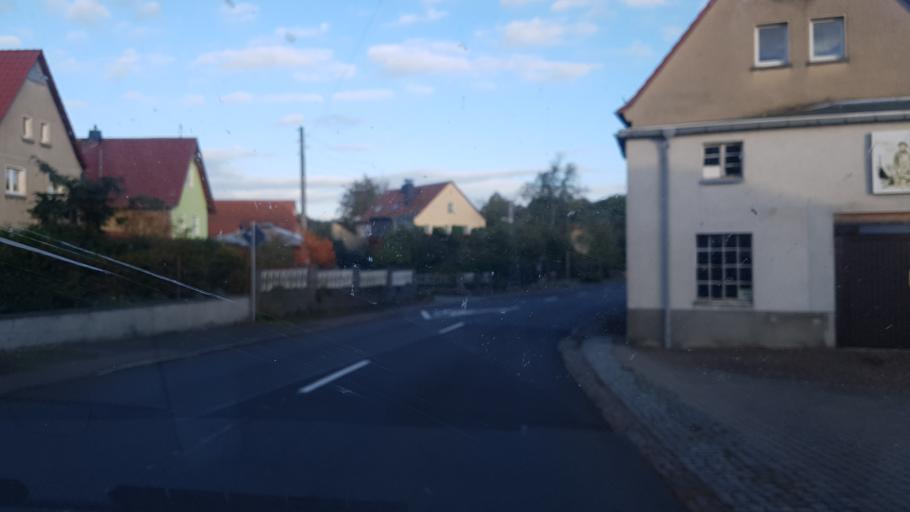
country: DE
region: Saxony
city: Dahlen
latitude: 51.3378
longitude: 13.0324
